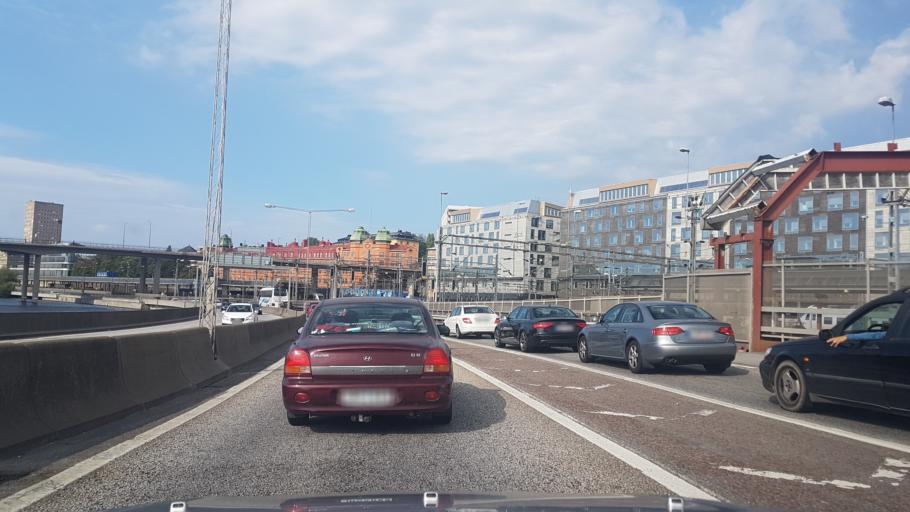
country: SE
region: Stockholm
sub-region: Stockholms Kommun
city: Stockholm
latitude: 59.3341
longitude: 18.0505
